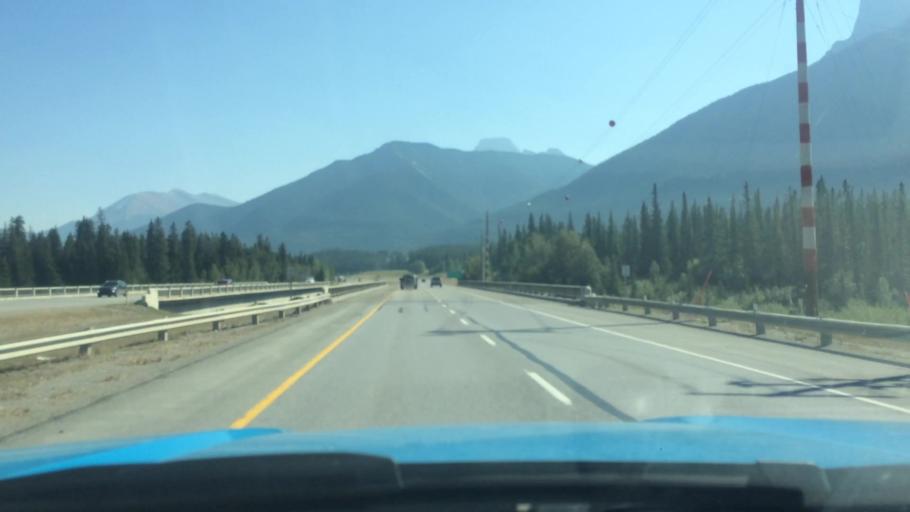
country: CA
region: Alberta
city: Canmore
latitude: 51.0641
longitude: -115.3239
